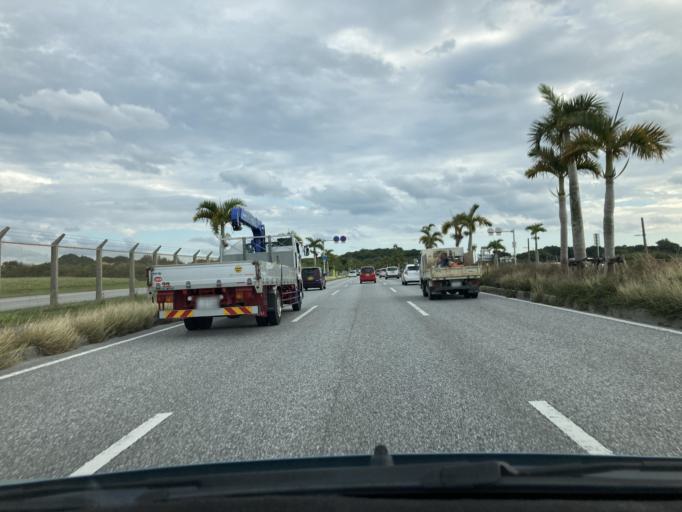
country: JP
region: Okinawa
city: Chatan
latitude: 26.3413
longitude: 127.7497
